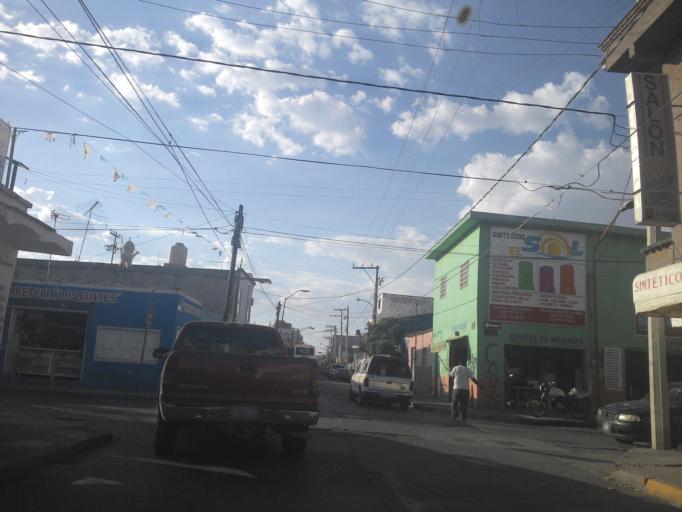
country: MX
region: Guanajuato
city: San Francisco del Rincon
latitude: 21.0144
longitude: -101.8547
